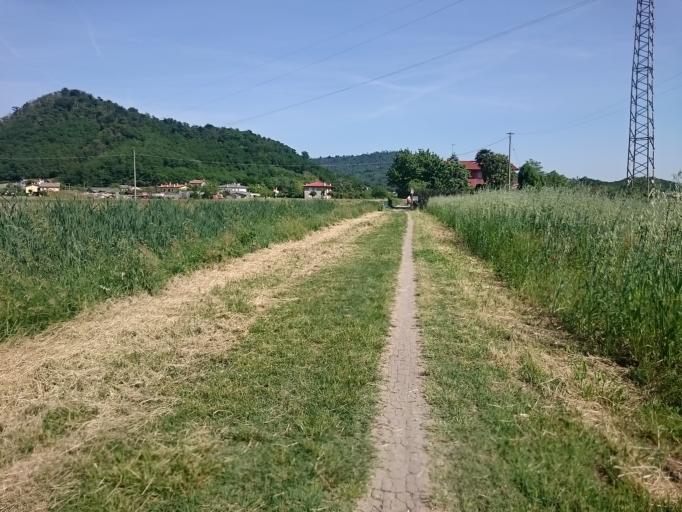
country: IT
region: Veneto
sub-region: Provincia di Padova
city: Treponti
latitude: 45.3706
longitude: 11.7004
